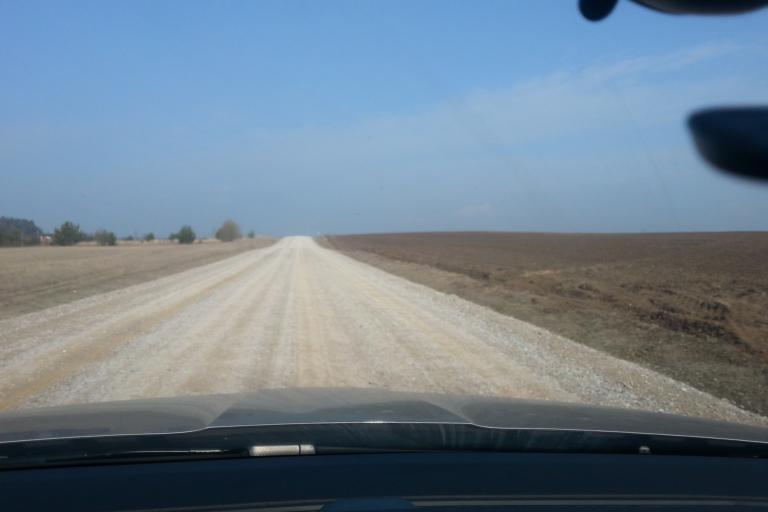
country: LT
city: Trakai
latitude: 54.5894
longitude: 24.9771
